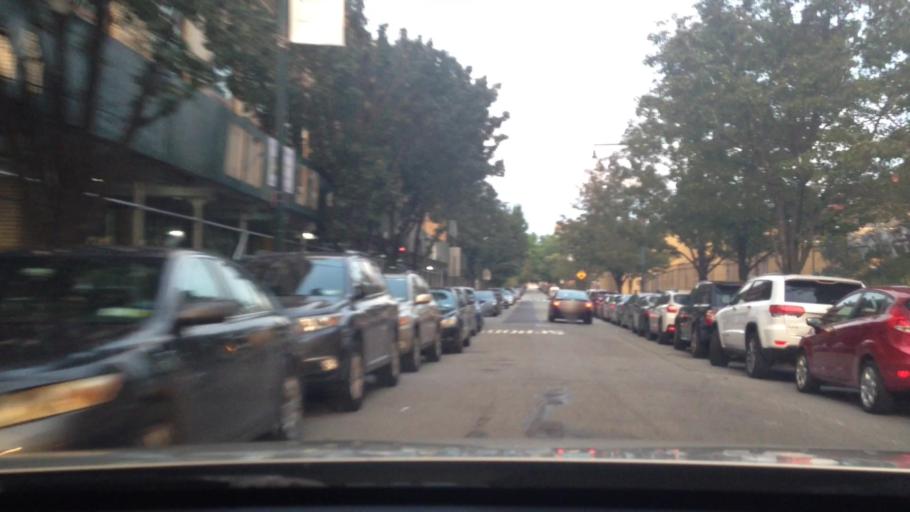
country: US
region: New York
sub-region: Queens County
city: Long Island City
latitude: 40.7442
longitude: -73.9580
